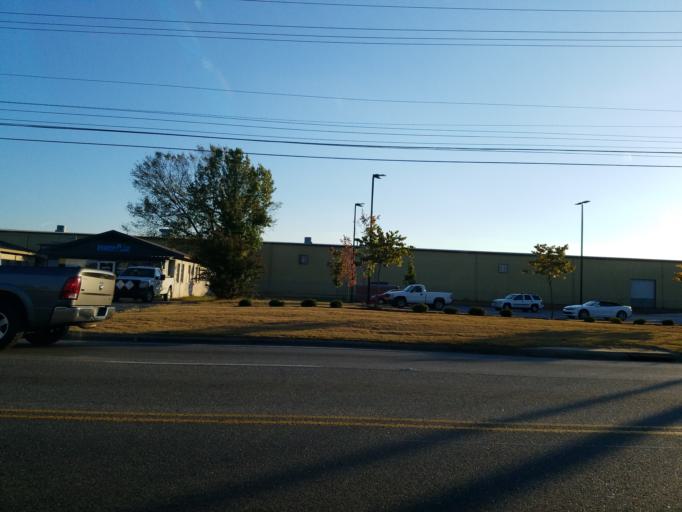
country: US
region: Georgia
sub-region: Gordon County
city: Calhoun
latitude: 34.4801
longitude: -84.9405
